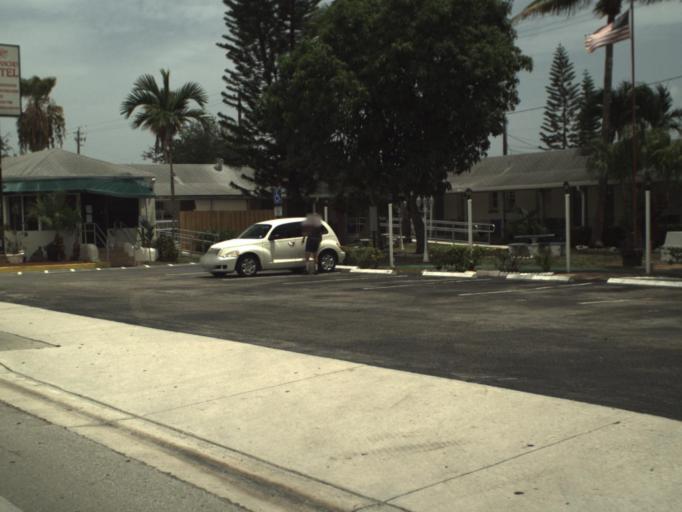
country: US
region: Florida
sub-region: Broward County
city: Hallandale Beach
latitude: 25.9910
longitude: -80.1425
